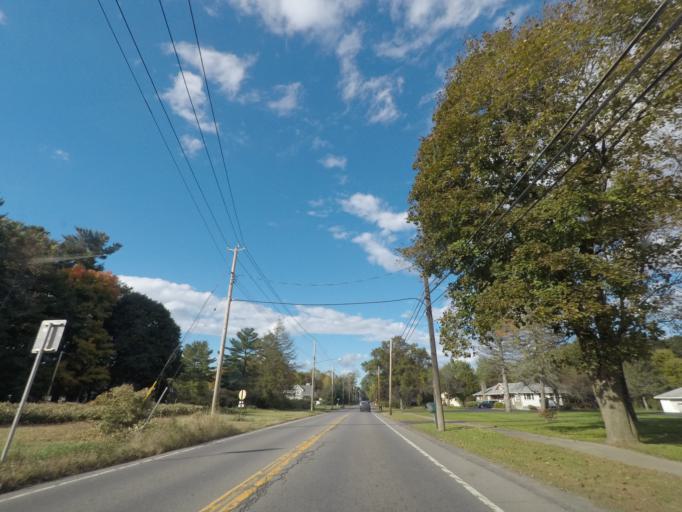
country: US
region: New York
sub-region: Schenectady County
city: Rotterdam
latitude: 42.7508
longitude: -73.9426
